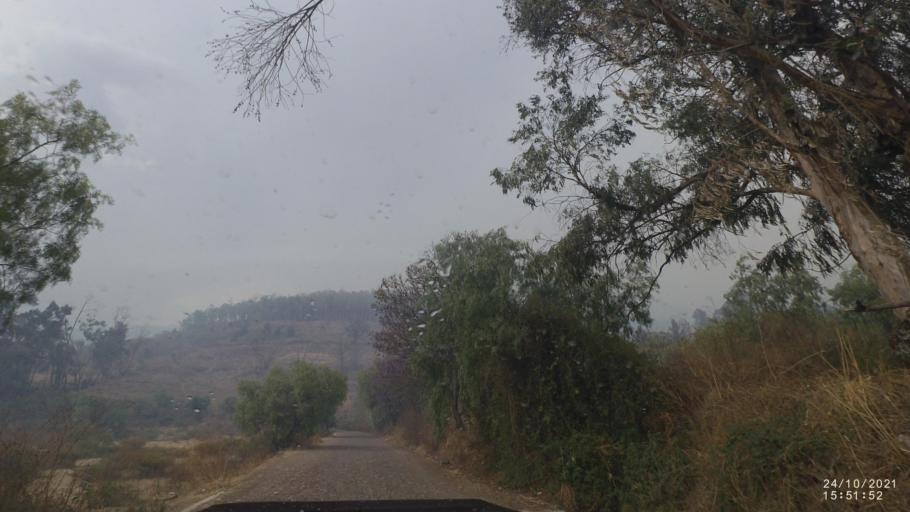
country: BO
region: Cochabamba
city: Cochabamba
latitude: -17.3494
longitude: -66.1488
